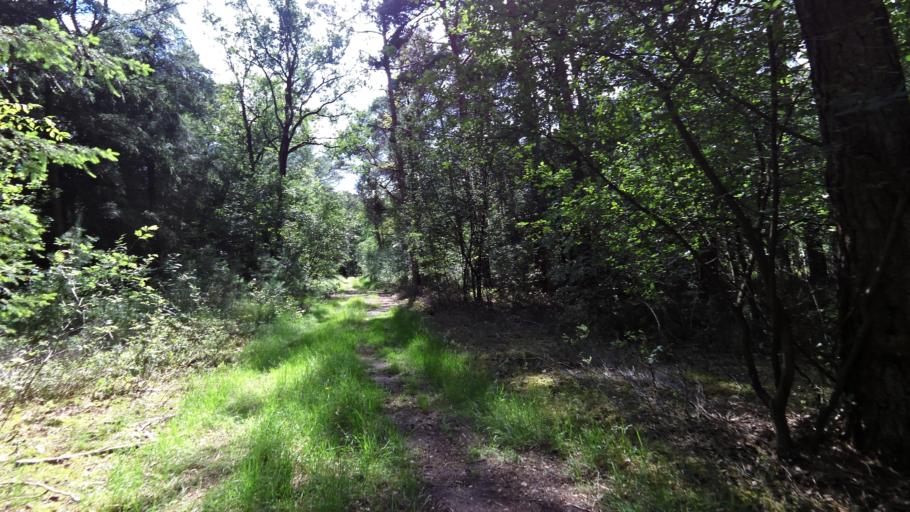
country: NL
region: Gelderland
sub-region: Gemeente Epe
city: Vaassen
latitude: 52.2683
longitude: 5.9306
